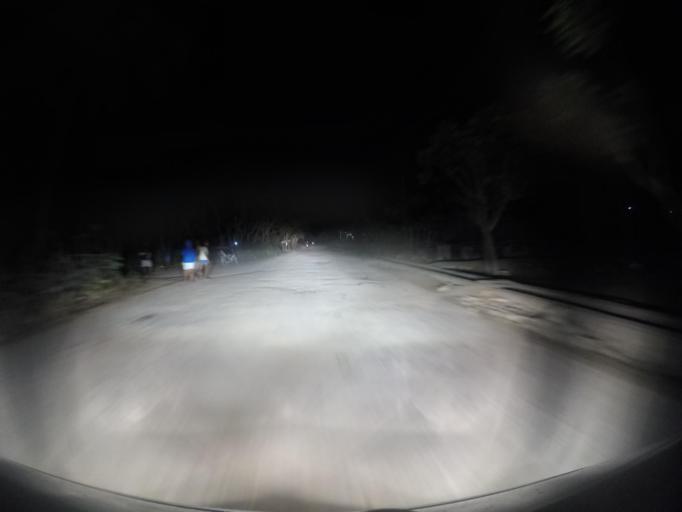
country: TL
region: Viqueque
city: Viqueque
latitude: -8.8020
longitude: 126.5506
